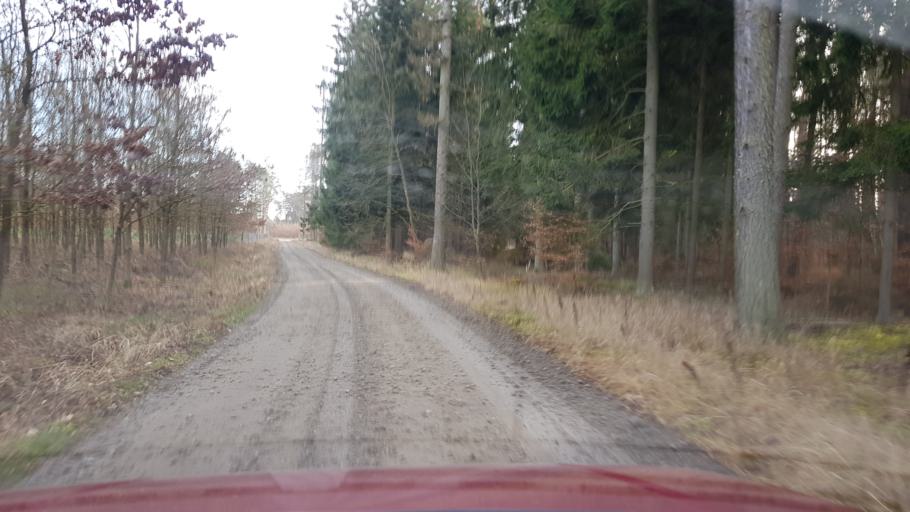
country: PL
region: West Pomeranian Voivodeship
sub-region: Powiat choszczenski
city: Pelczyce
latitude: 52.9148
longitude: 15.3725
